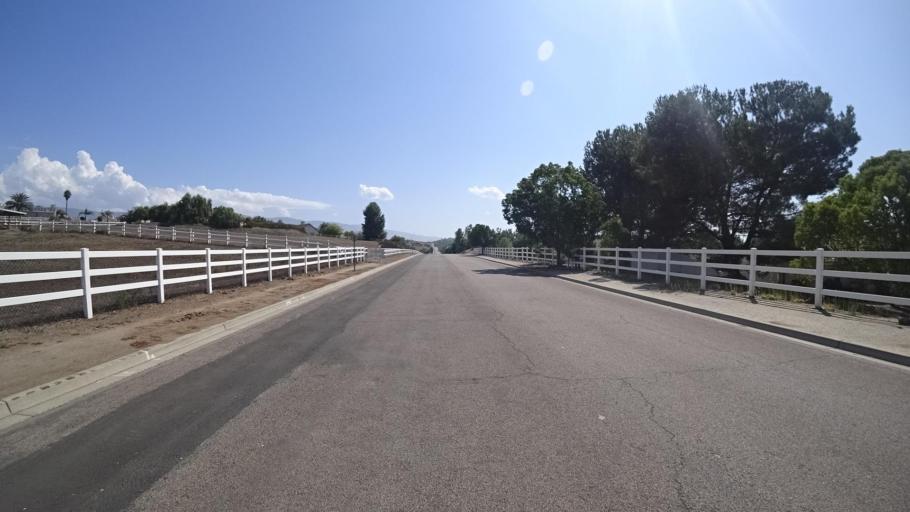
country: US
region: California
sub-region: San Diego County
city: Valley Center
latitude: 33.2820
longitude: -117.0217
